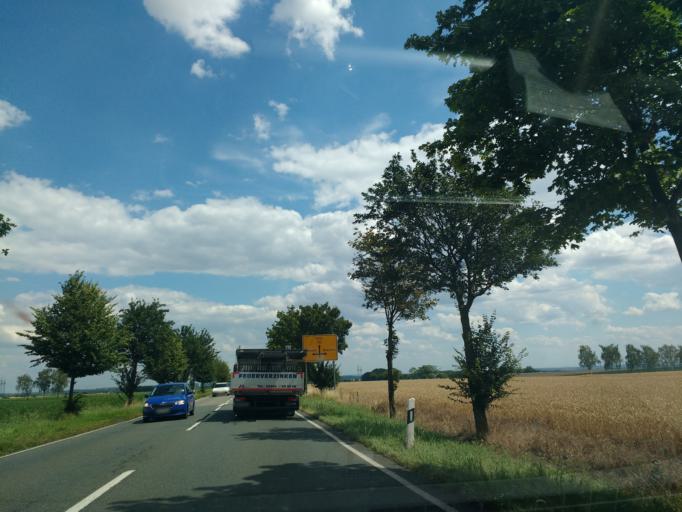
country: DE
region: Saxony-Anhalt
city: Droyssig
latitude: 51.0728
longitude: 12.0054
